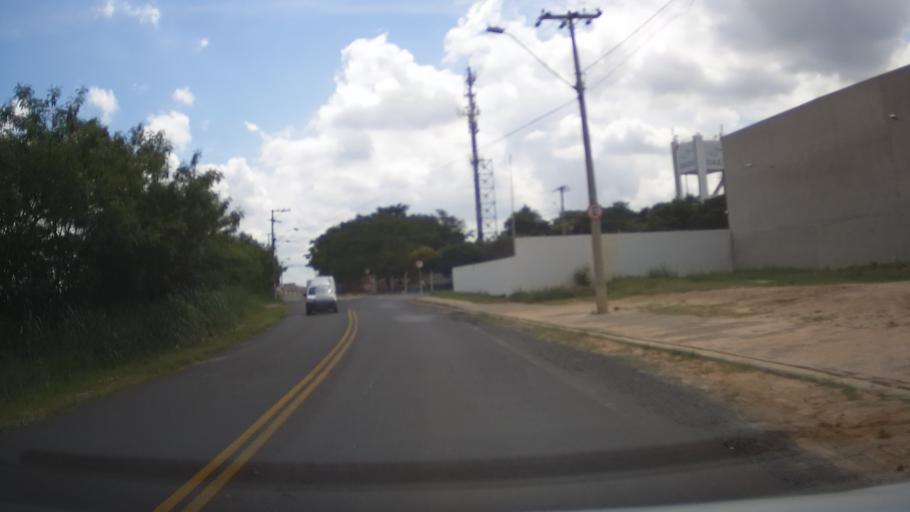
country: BR
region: Sao Paulo
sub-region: Valinhos
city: Valinhos
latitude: -22.9695
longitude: -46.9805
